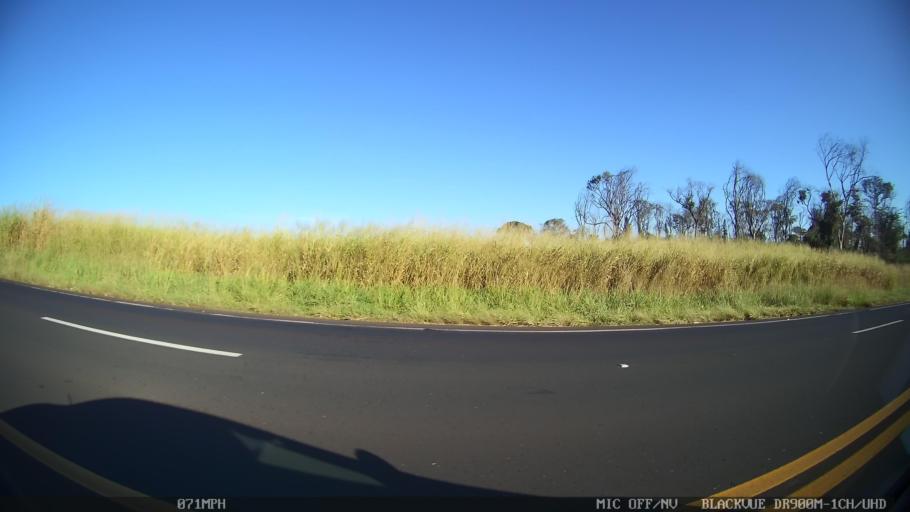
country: BR
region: Sao Paulo
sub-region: Guapiacu
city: Guapiacu
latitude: -20.7419
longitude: -49.1005
